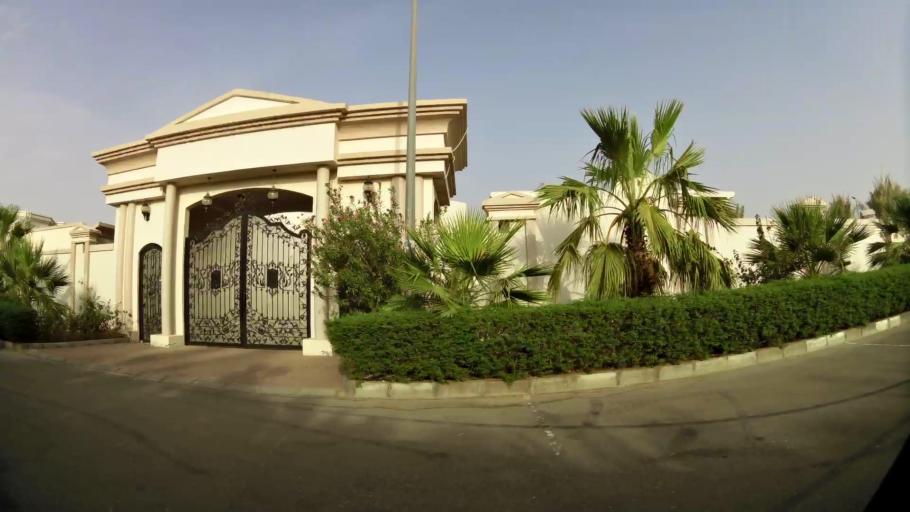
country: AE
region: Abu Dhabi
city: Al Ain
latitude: 24.1225
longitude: 55.7087
